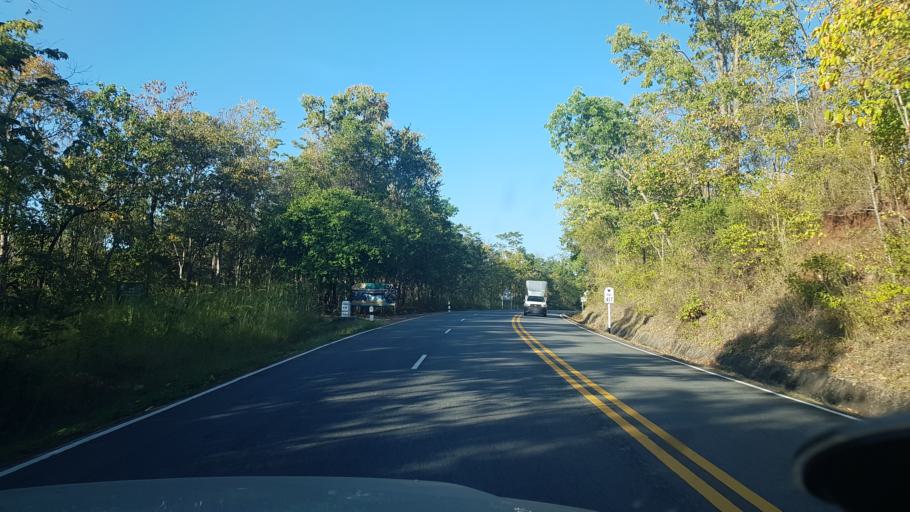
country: TH
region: Phetchabun
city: Nam Nao
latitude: 16.7026
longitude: 101.6495
